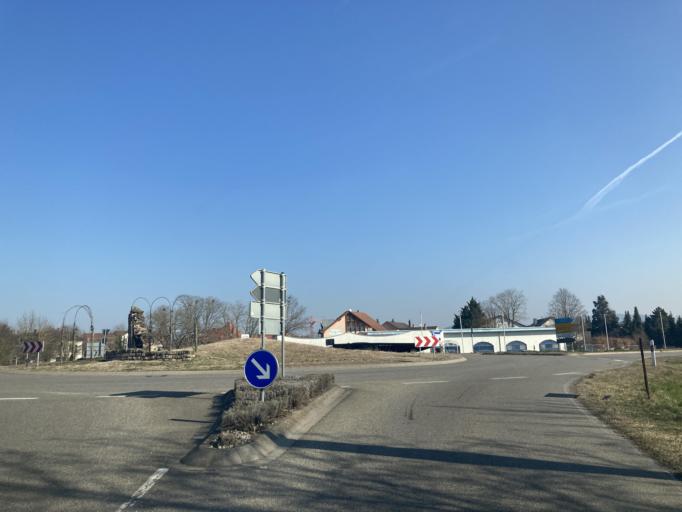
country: DE
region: Baden-Wuerttemberg
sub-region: Freiburg Region
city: Breisach am Rhein
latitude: 48.0248
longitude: 7.5884
